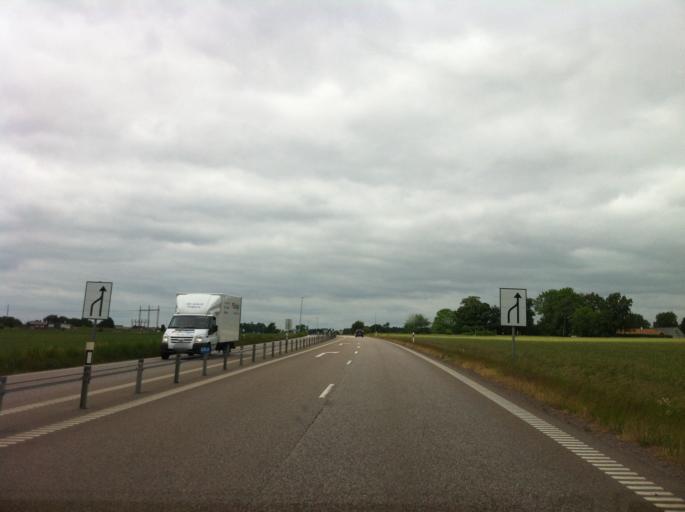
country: SE
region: Skane
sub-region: Eslovs Kommun
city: Eslov
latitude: 55.7977
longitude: 13.3917
